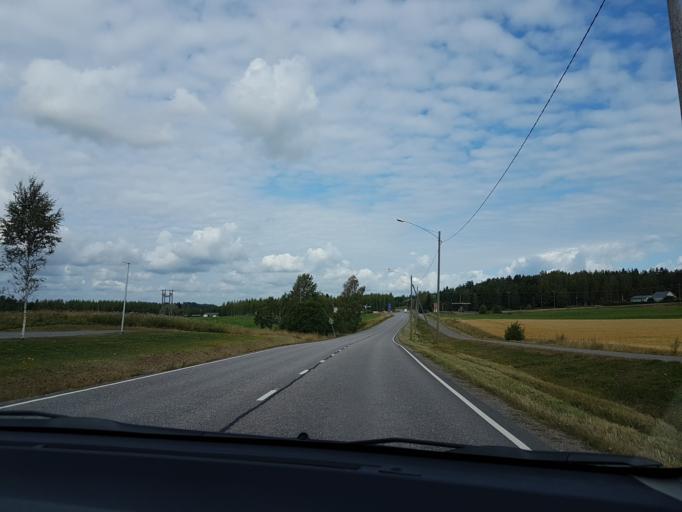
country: FI
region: Uusimaa
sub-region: Helsinki
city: Pornainen
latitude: 60.4810
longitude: 25.3715
